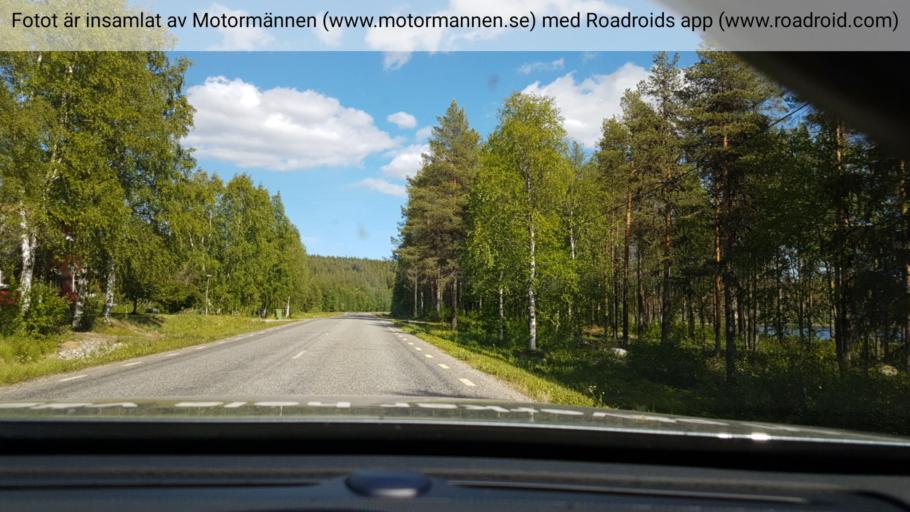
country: SE
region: Vaesterbotten
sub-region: Lycksele Kommun
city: Lycksele
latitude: 64.5901
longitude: 18.5968
